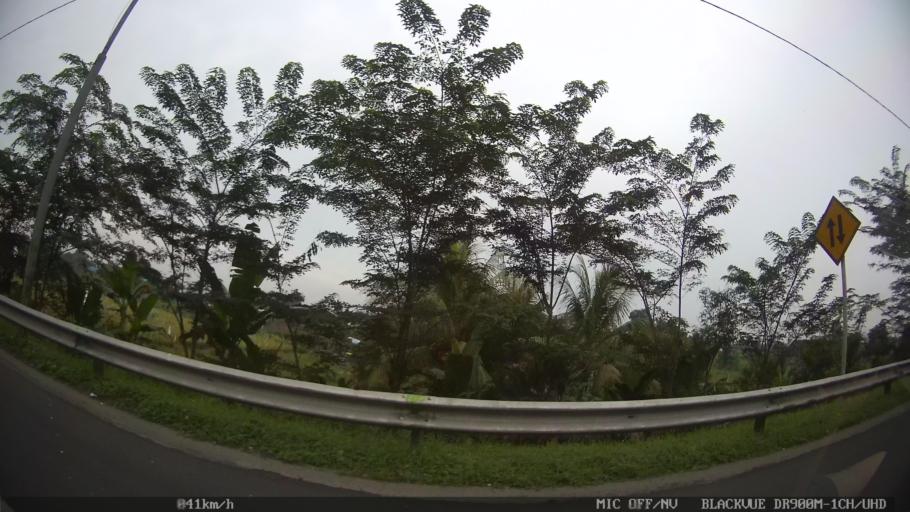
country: ID
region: North Sumatra
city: Deli Tua
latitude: 3.5462
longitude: 98.7259
